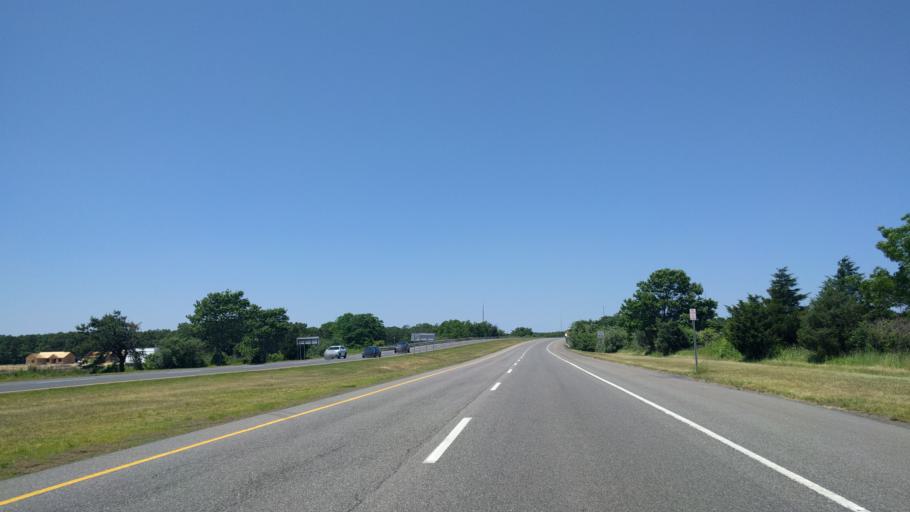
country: US
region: New York
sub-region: Suffolk County
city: Eastport
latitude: 40.8458
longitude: -72.7306
